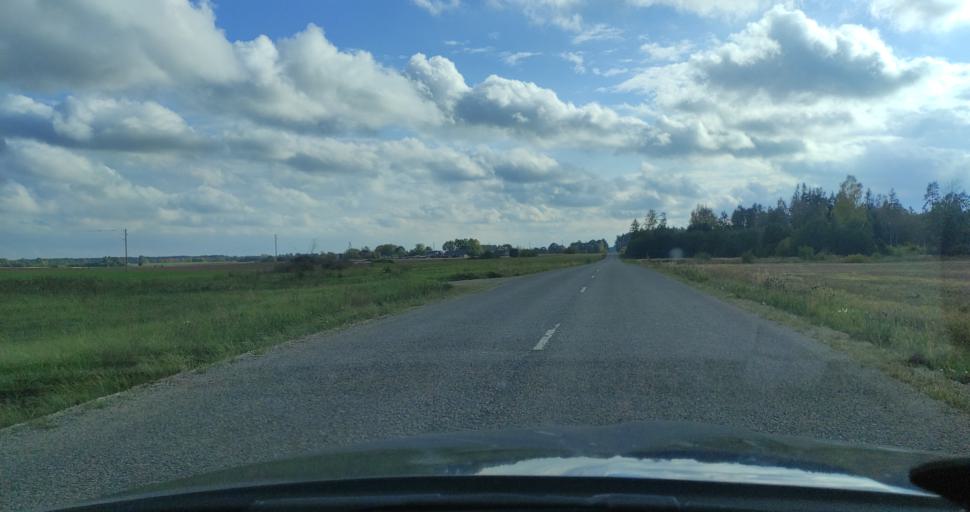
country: LV
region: Talsu Rajons
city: Sabile
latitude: 56.9157
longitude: 22.3974
